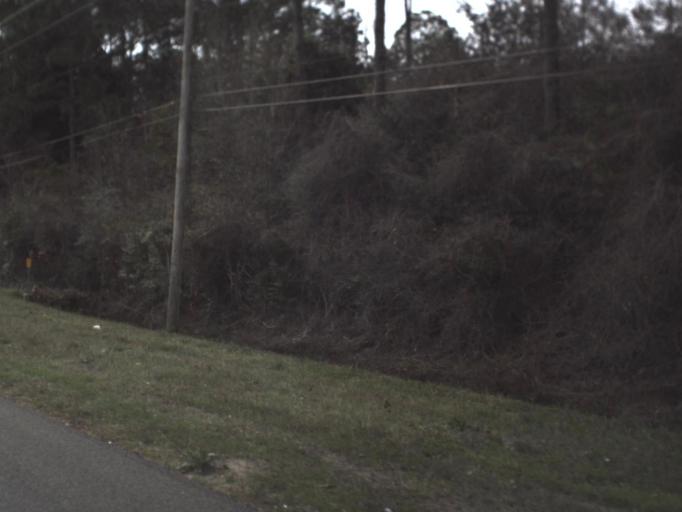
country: US
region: Florida
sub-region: Bay County
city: Hiland Park
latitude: 30.2115
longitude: -85.6100
